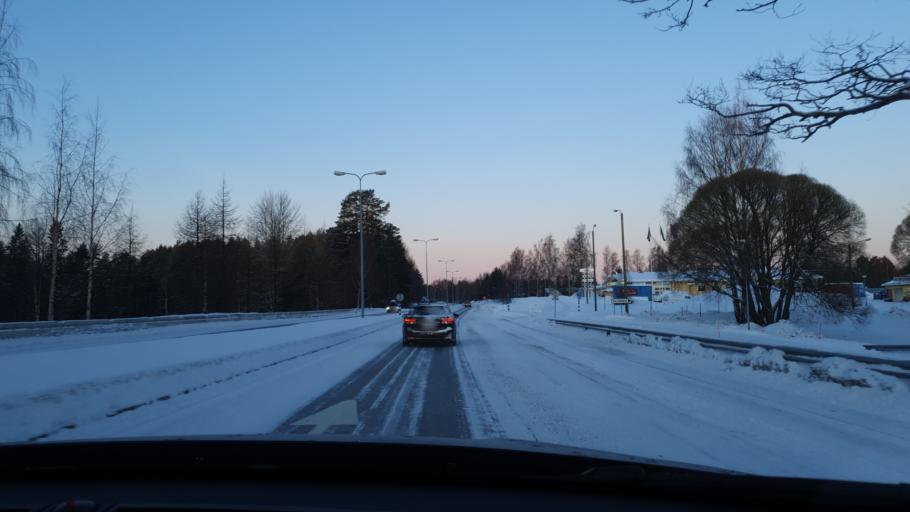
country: FI
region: Kainuu
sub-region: Kajaani
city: Vuokatti
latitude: 64.1376
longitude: 28.3350
